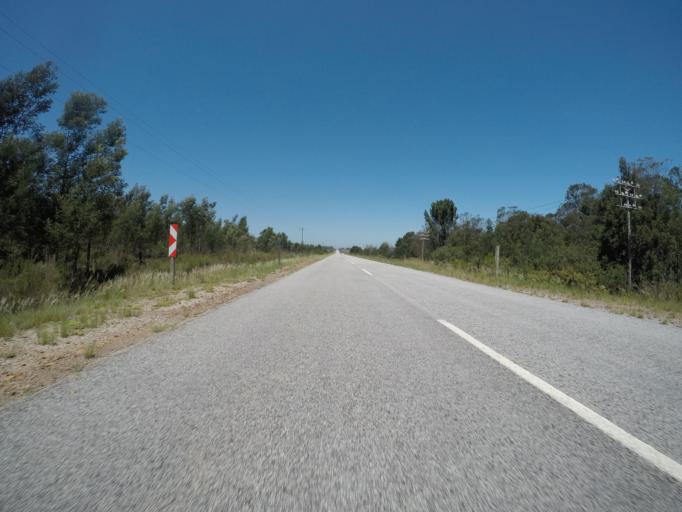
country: ZA
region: Eastern Cape
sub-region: Cacadu District Municipality
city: Kareedouw
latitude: -33.9639
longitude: 24.4361
